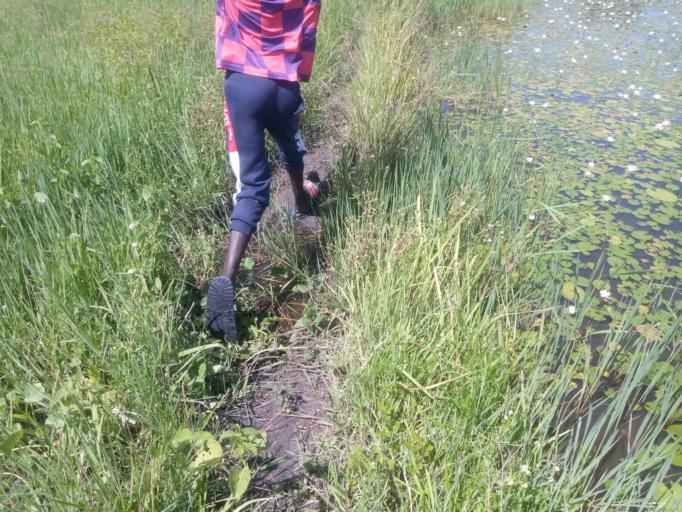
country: GM
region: Western
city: Gunjur
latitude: 13.0371
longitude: -16.7316
